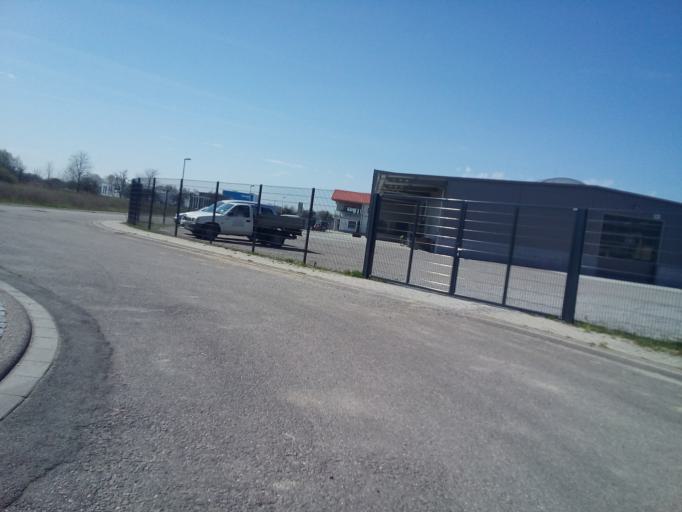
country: DE
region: Baden-Wuerttemberg
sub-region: Freiburg Region
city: Rheinau
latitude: 48.6762
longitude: 7.9324
